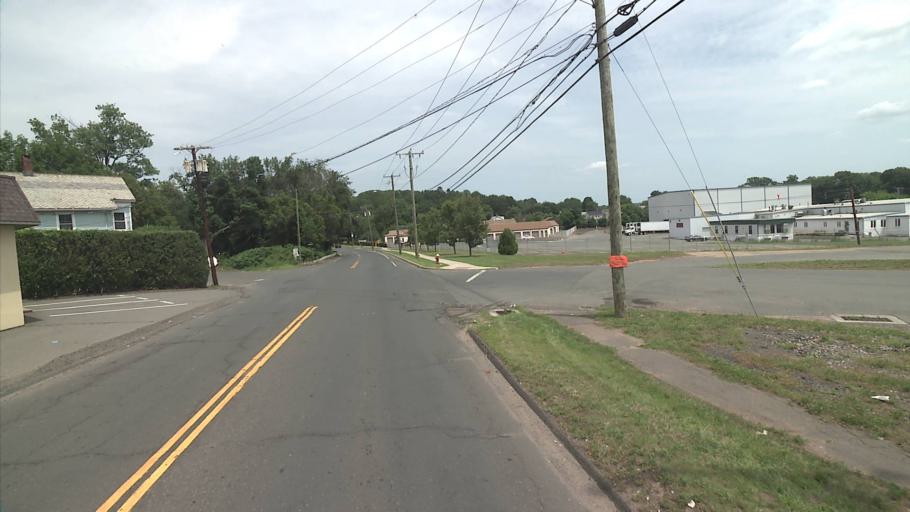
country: US
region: Connecticut
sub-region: New Haven County
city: Meriden
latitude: 41.5410
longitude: -72.8165
